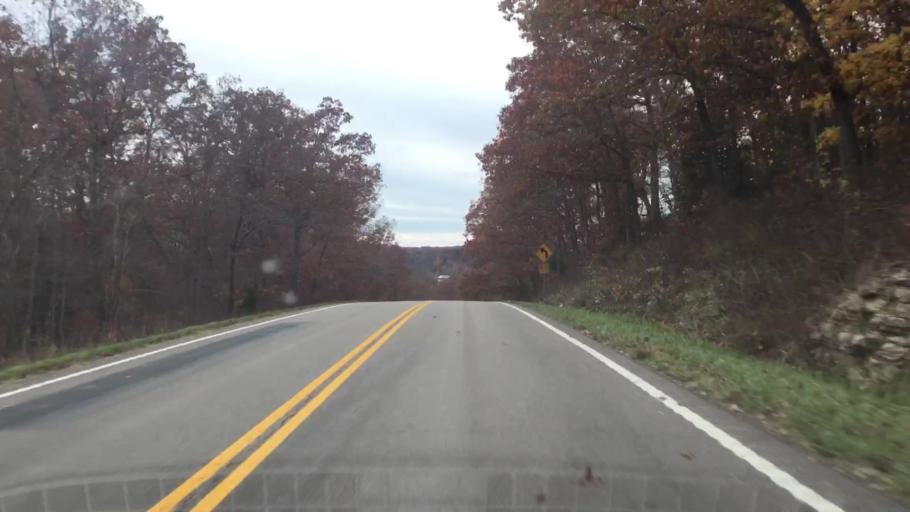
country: US
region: Missouri
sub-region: Gasconade County
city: Hermann
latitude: 38.7198
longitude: -91.6479
